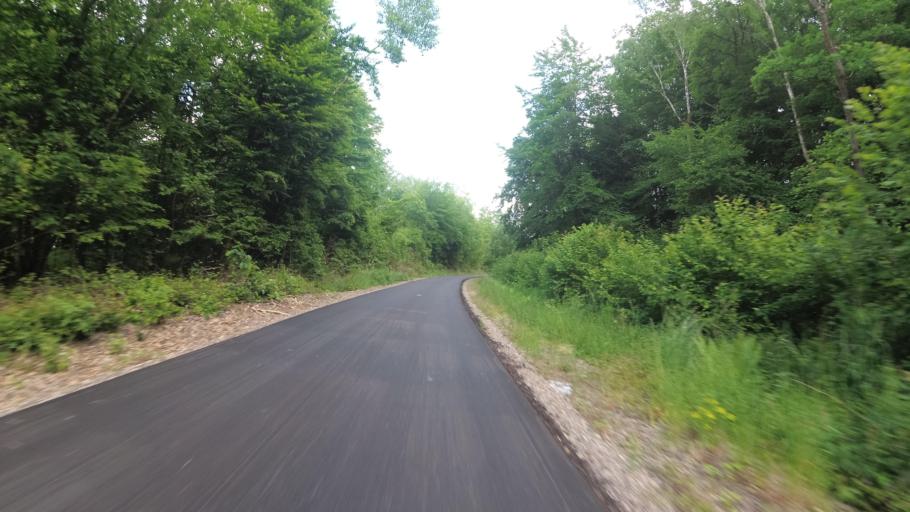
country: DE
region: Rheinland-Pfalz
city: Achtelsbach
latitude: 49.5828
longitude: 7.0783
